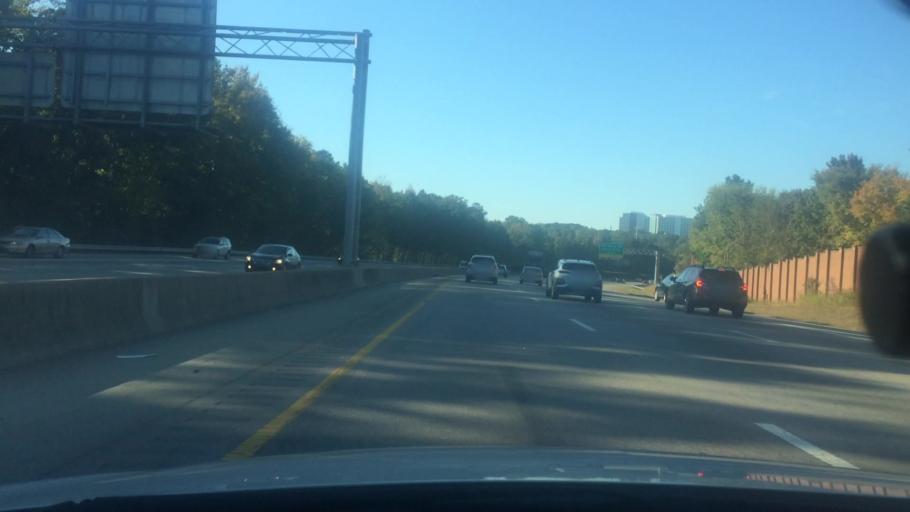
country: US
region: North Carolina
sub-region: Wake County
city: West Raleigh
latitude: 35.8267
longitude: -78.6243
